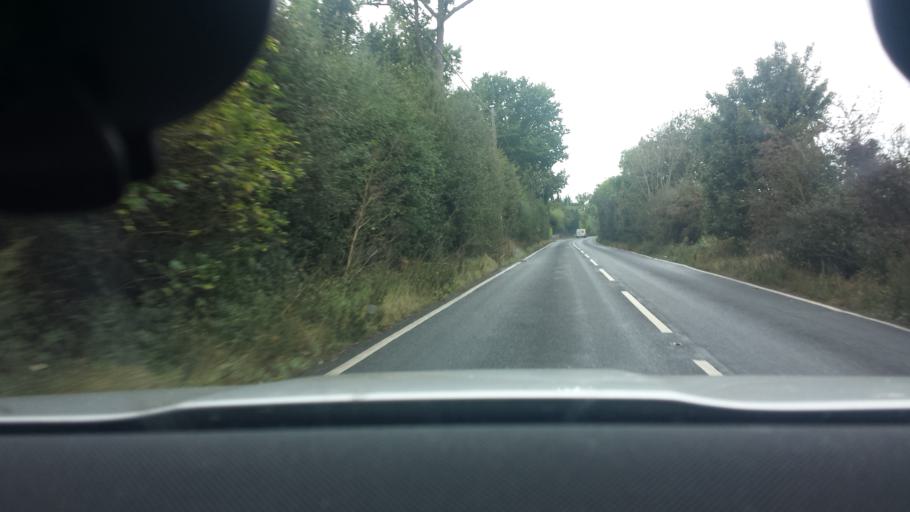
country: GB
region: England
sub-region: Kent
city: Staplehurst
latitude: 51.1813
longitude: 0.5507
